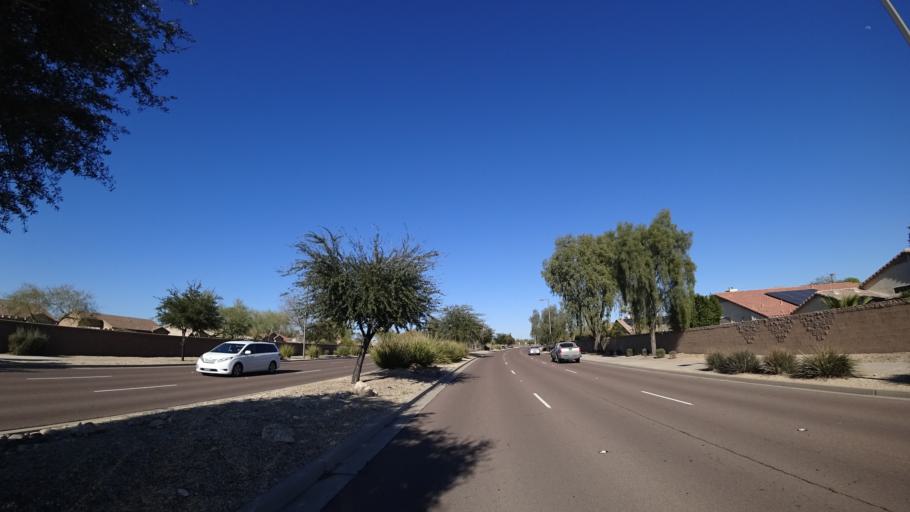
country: US
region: Arizona
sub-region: Maricopa County
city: Sun City West
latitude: 33.6433
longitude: -112.3928
